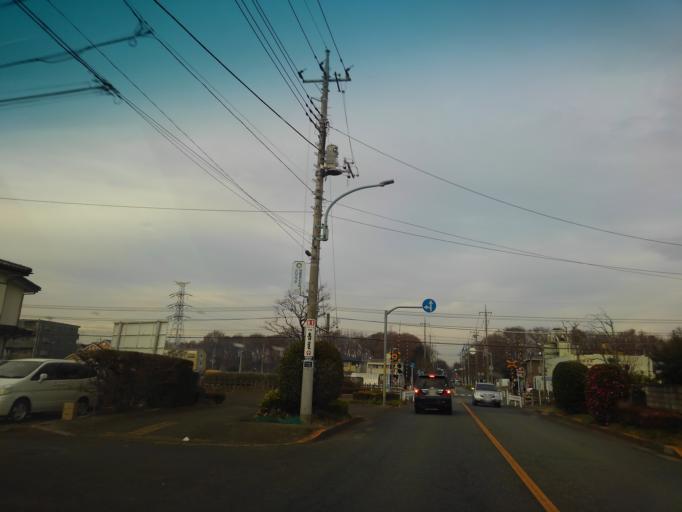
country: JP
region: Tokyo
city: Higashimurayama-shi
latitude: 35.7330
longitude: 139.4444
